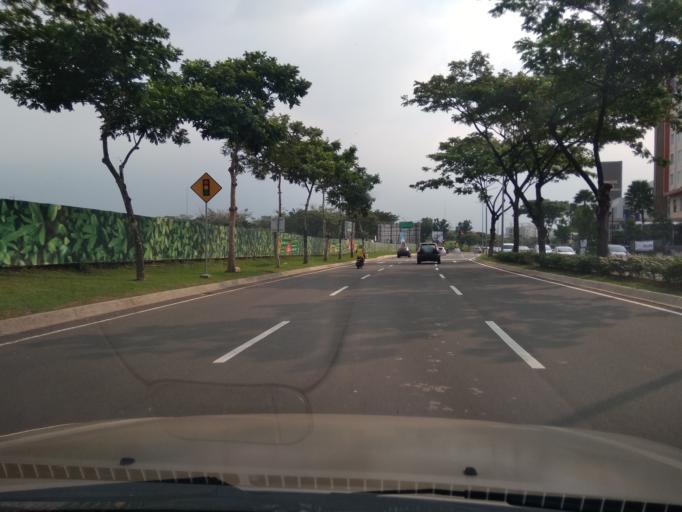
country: ID
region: West Java
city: Serpong
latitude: -6.2892
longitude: 106.6513
